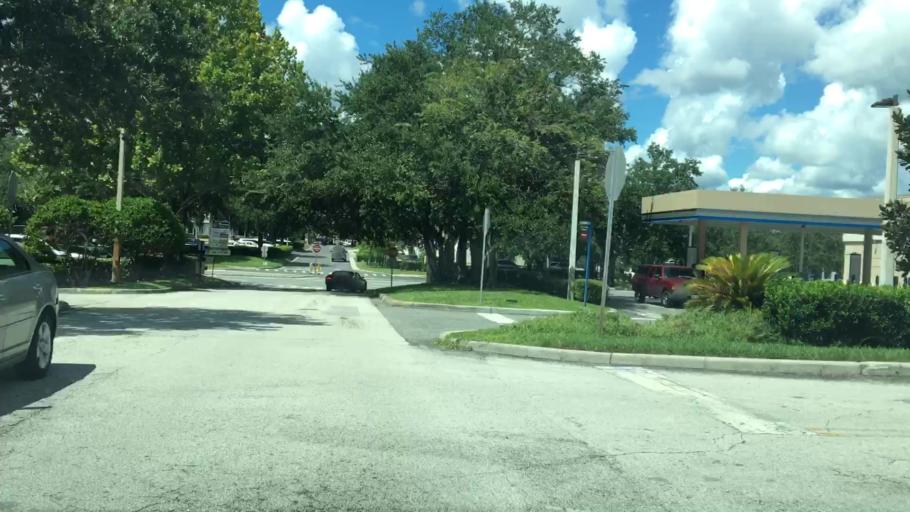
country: US
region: Florida
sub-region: Seminole County
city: Heathrow
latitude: 28.7553
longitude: -81.3516
